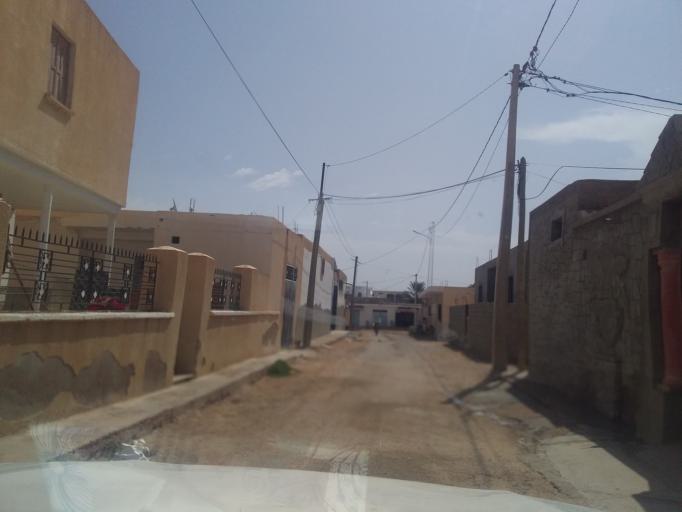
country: TN
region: Madanin
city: Medenine
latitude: 33.5832
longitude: 10.3202
